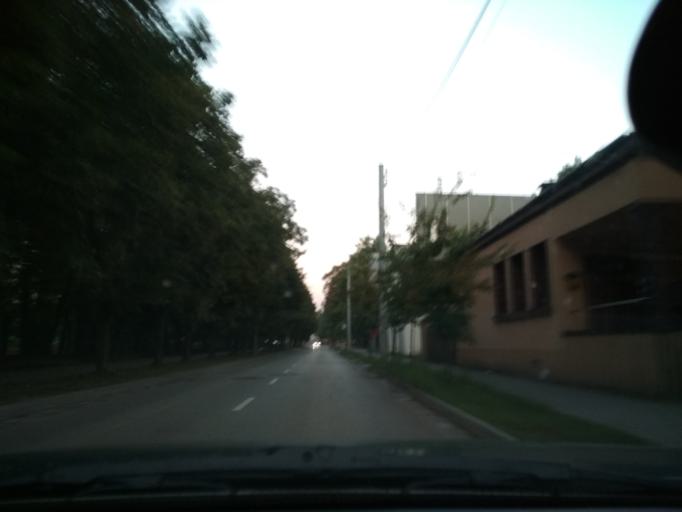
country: PL
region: Silesian Voivodeship
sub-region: Powiat zawiercianski
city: Zawiercie
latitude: 50.4868
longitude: 19.4302
